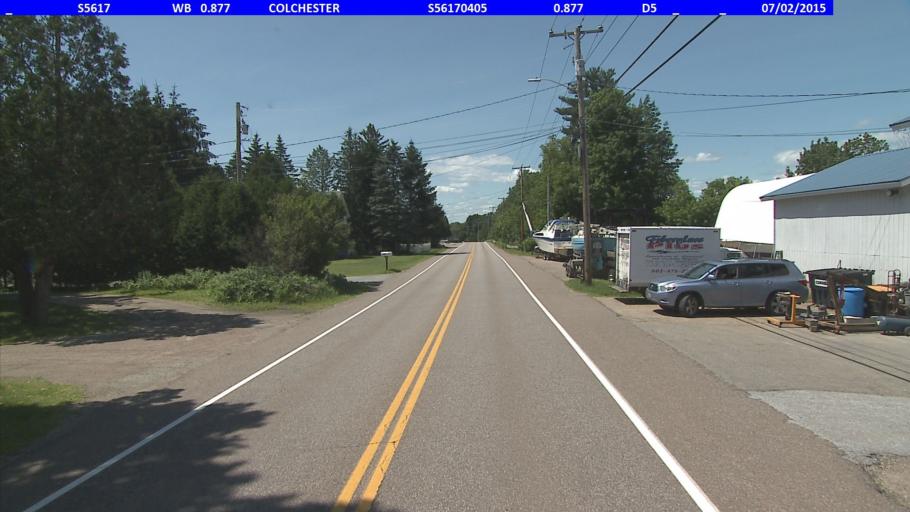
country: US
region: Vermont
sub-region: Chittenden County
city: Colchester
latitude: 44.5507
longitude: -73.1747
